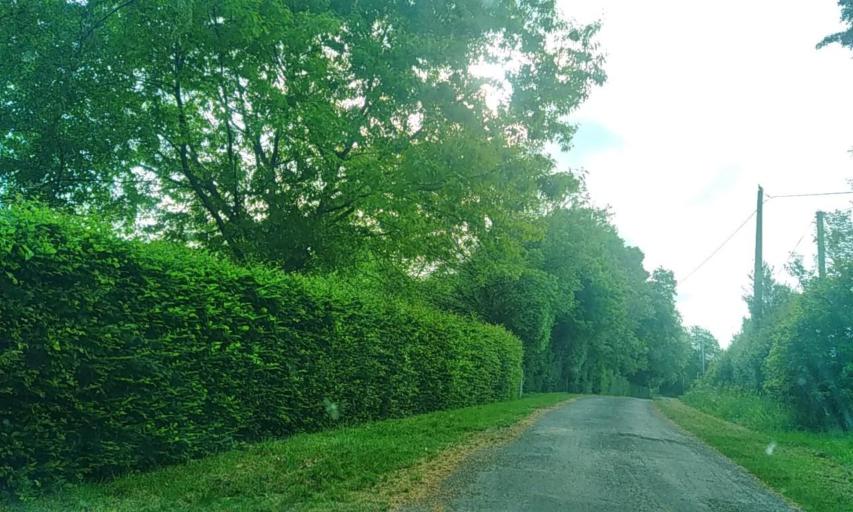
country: FR
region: Poitou-Charentes
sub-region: Departement des Deux-Sevres
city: Boisme
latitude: 46.7603
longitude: -0.4412
